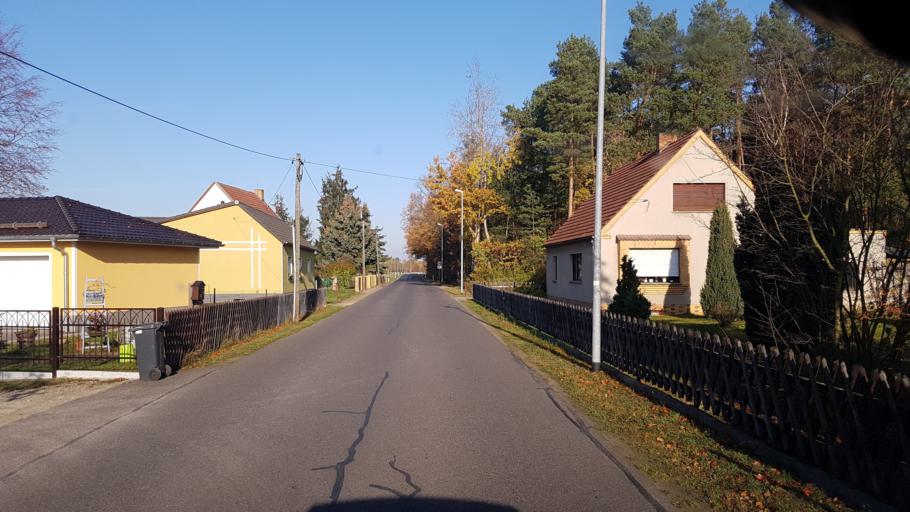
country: DE
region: Brandenburg
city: Schipkau
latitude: 51.5556
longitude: 13.9279
